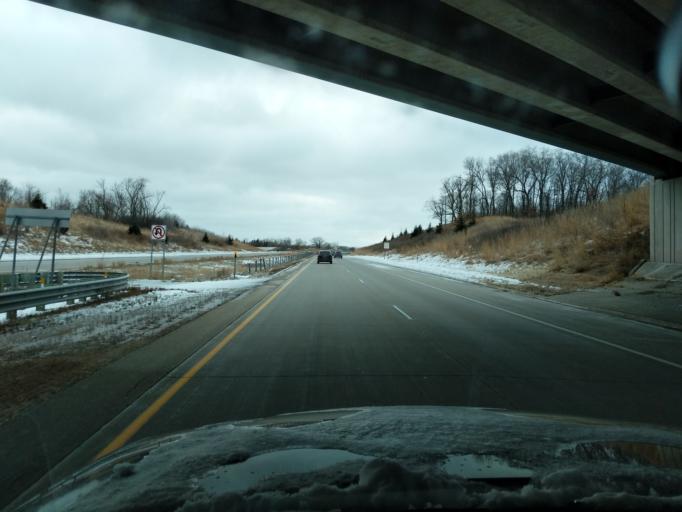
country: US
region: Minnesota
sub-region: Scott County
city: Shakopee
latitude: 44.8279
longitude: -93.5602
